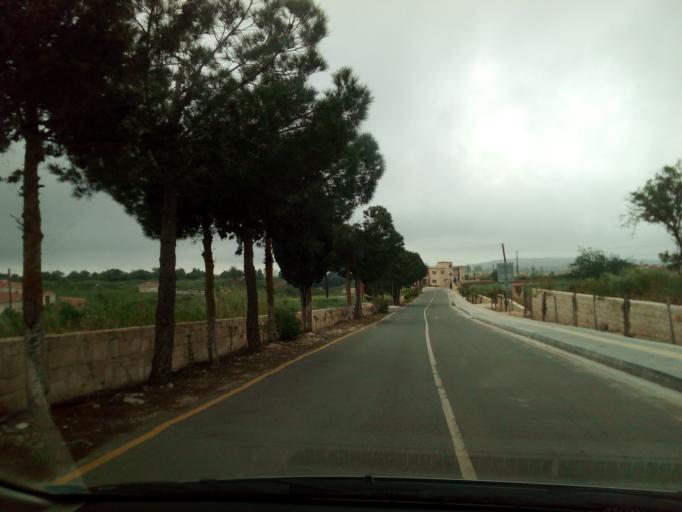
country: CY
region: Pafos
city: Pegeia
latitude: 34.9110
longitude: 32.4233
